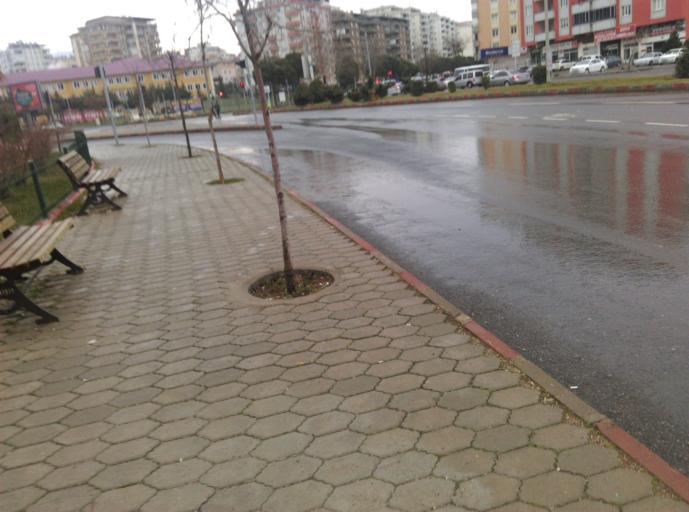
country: TR
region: Kahramanmaras
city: Kahramanmaras
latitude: 37.5836
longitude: 36.8897
